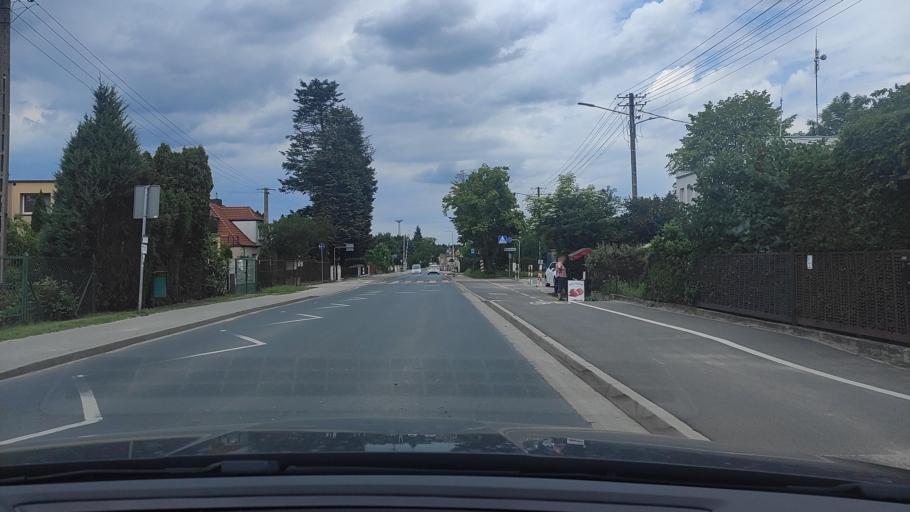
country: PL
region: Greater Poland Voivodeship
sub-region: Powiat poznanski
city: Kostrzyn
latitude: 52.4654
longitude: 17.1697
